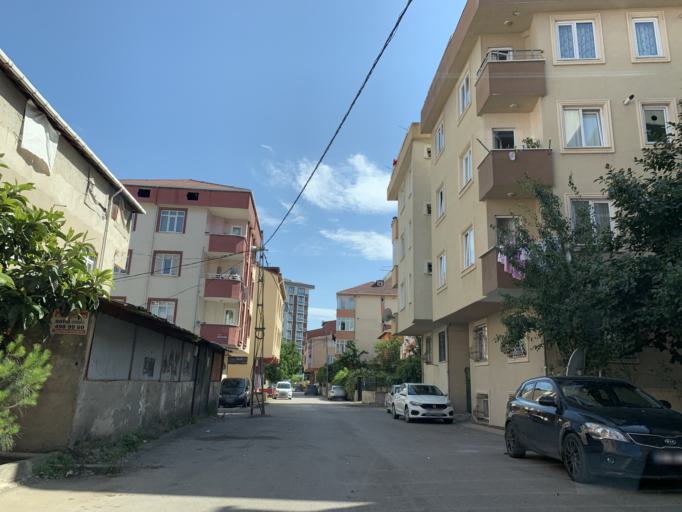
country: TR
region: Istanbul
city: Pendik
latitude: 40.8915
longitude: 29.2718
